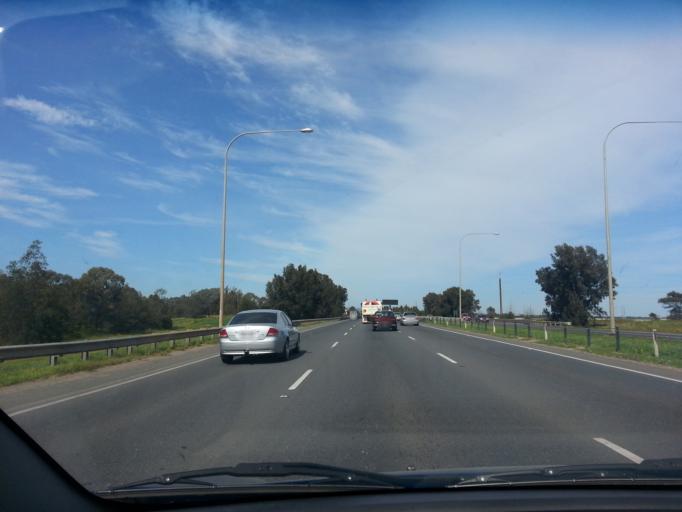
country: AU
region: South Australia
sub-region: Salisbury
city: Salisbury
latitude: -34.7999
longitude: 138.5967
